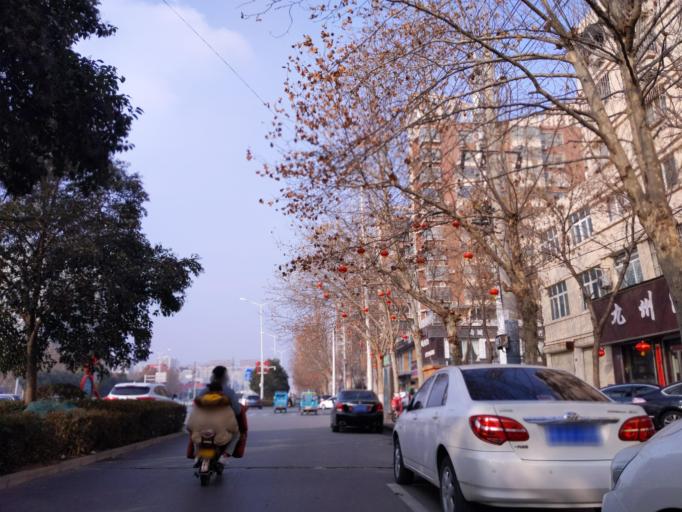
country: CN
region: Henan Sheng
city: Puyang
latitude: 35.7841
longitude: 115.0210
